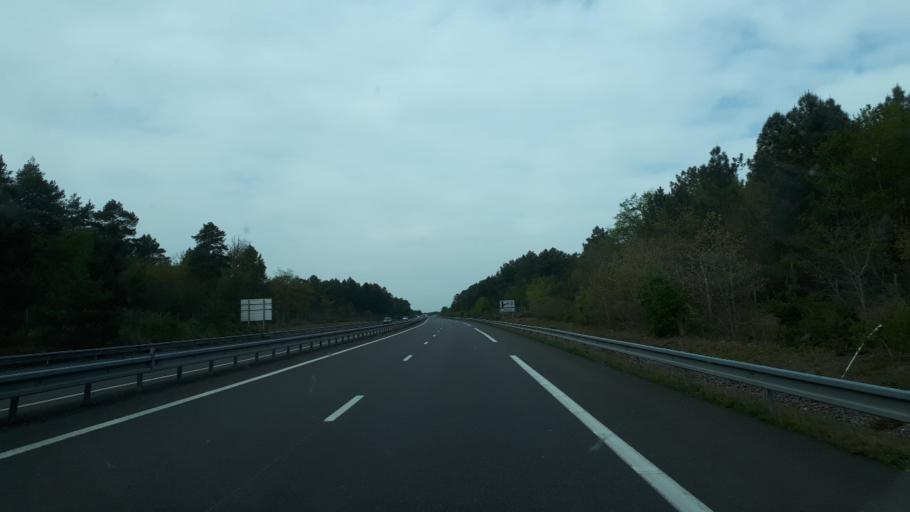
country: FR
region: Centre
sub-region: Departement du Loir-et-Cher
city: Selles-sur-Cher
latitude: 47.3359
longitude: 1.5314
